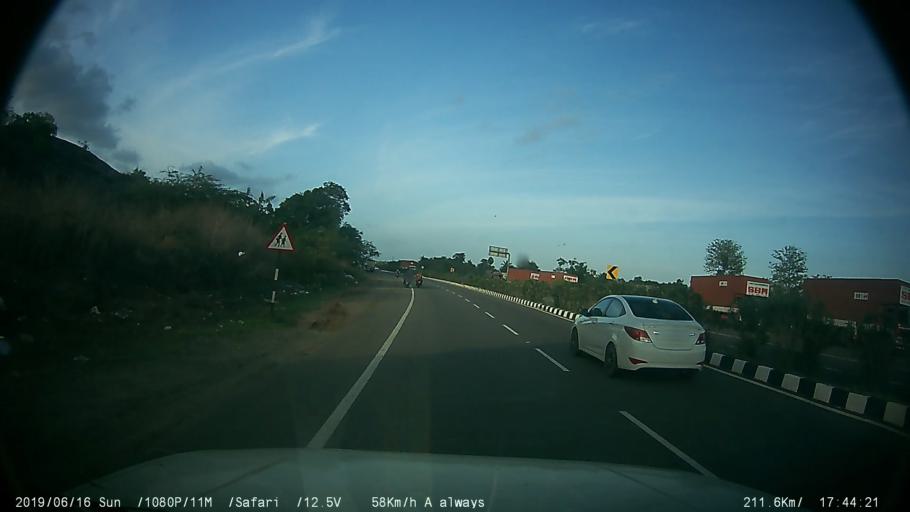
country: IN
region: Kerala
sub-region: Palakkad district
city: Chittur
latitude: 10.8171
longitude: 76.8043
